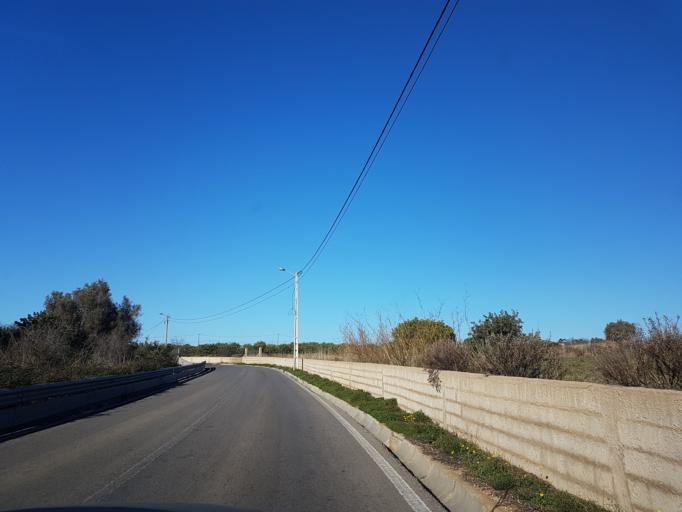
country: PT
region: Faro
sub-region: Lagoa
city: Lagoa
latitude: 37.1178
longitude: -8.4153
